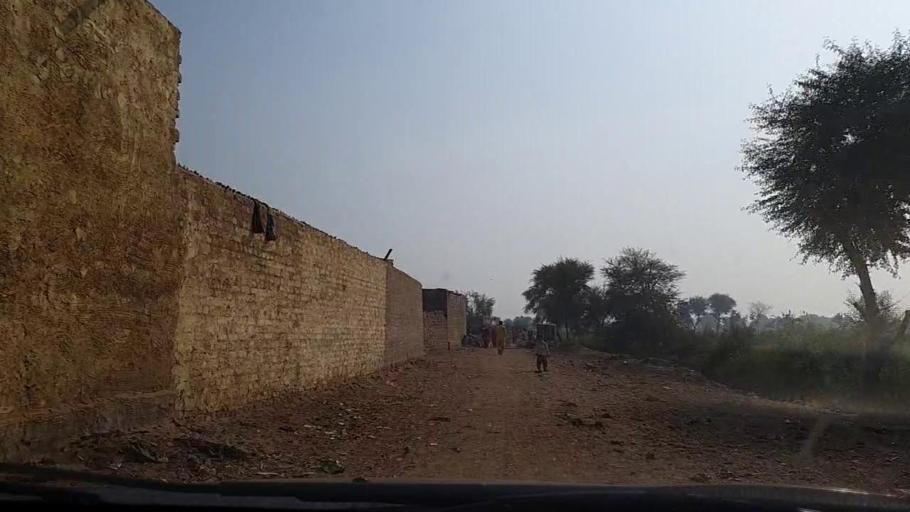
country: PK
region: Sindh
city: Sanghar
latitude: 26.0453
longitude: 68.9798
